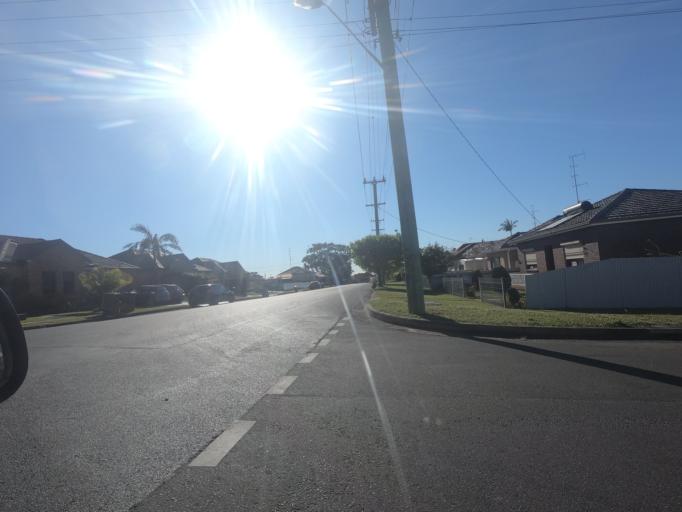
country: AU
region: New South Wales
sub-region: Wollongong
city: Corrimal
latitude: -34.3845
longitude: 150.8923
